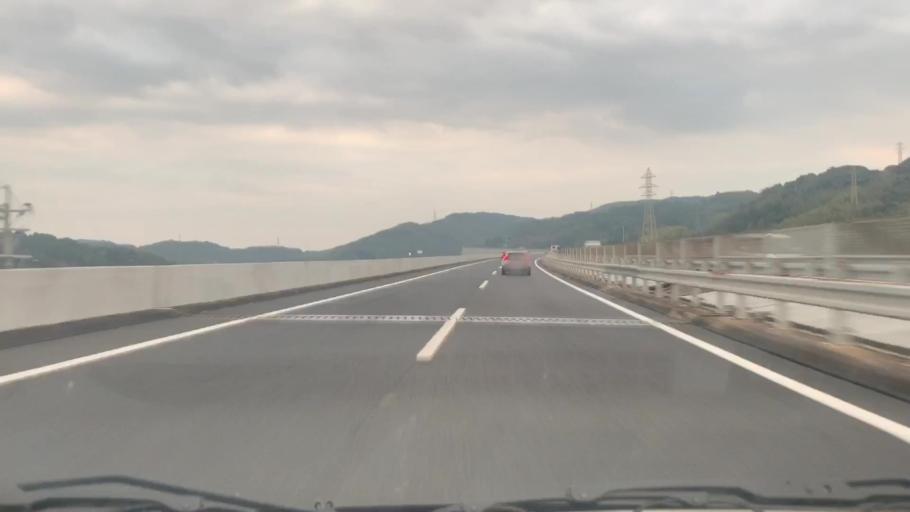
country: JP
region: Nagasaki
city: Omura
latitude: 32.8905
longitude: 129.9894
